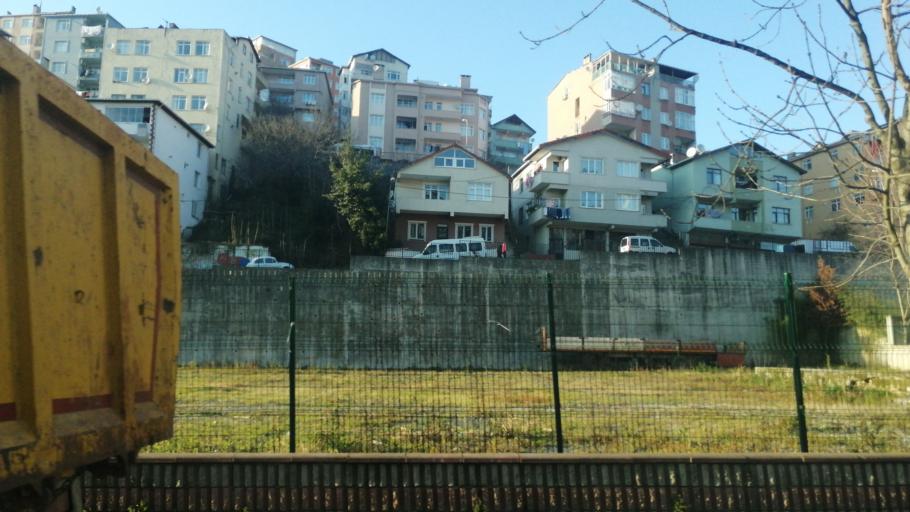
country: TR
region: Istanbul
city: UEskuedar
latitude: 41.0514
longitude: 29.0639
